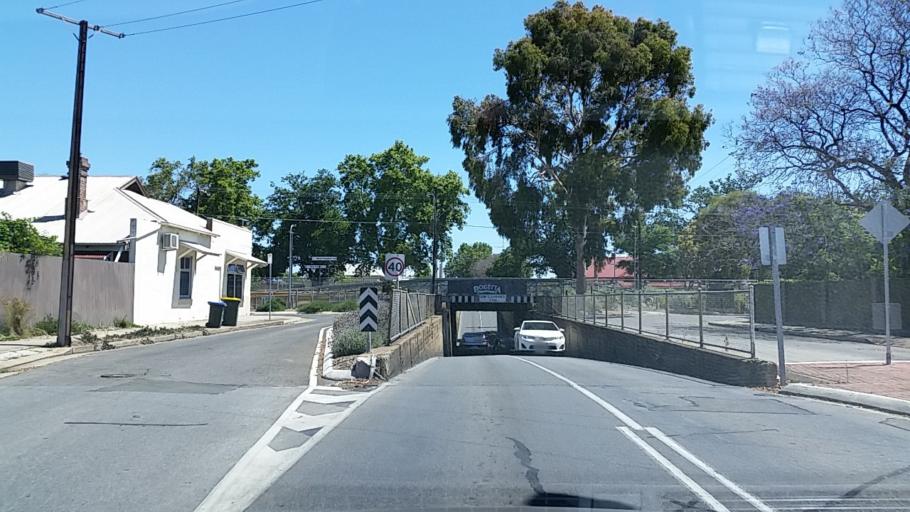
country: AU
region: South Australia
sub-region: Charles Sturt
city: Allenby Gardens
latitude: -34.8910
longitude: 138.5571
